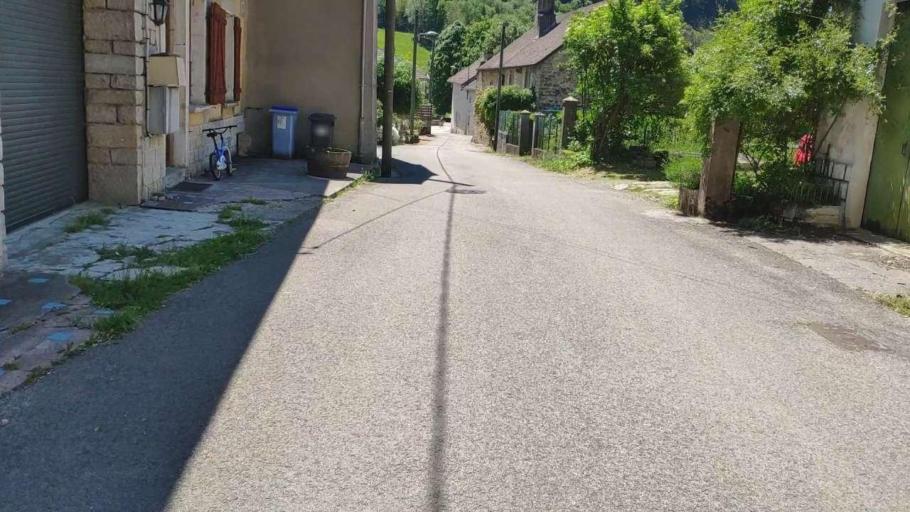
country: FR
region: Franche-Comte
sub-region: Departement du Jura
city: Poligny
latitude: 46.7495
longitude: 5.6704
